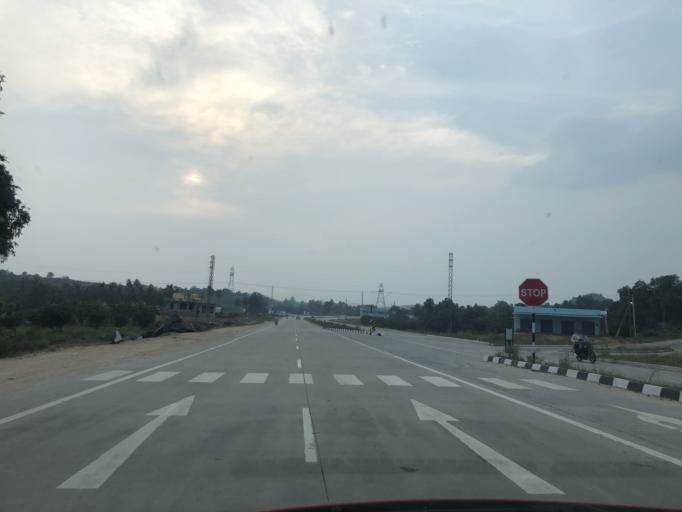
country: IN
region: Andhra Pradesh
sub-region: Chittoor
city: Chittoor
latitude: 13.1967
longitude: 78.9937
